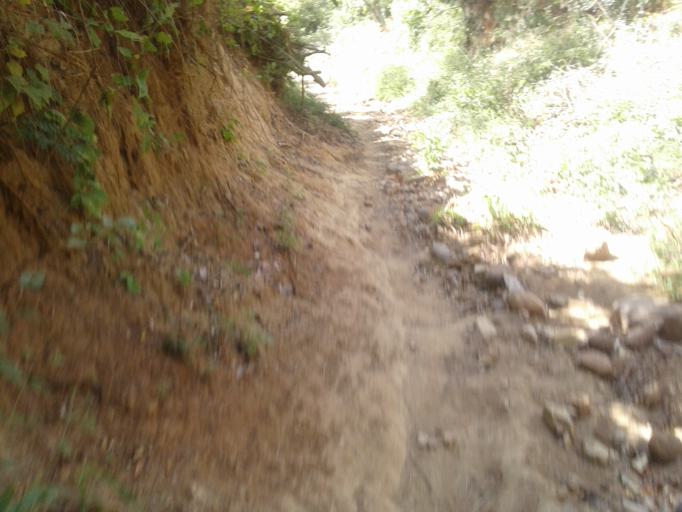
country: NI
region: Carazo
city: Santa Teresa
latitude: 11.6265
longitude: -86.1903
